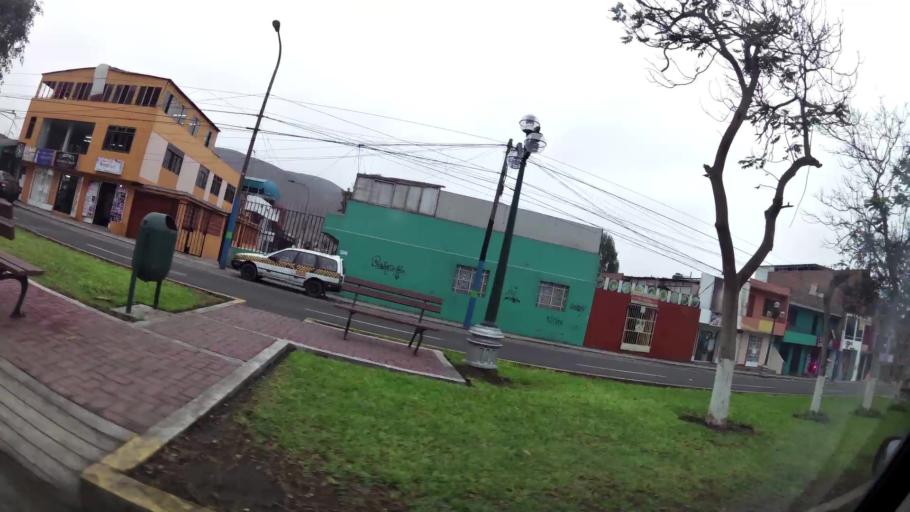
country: PE
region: Lima
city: Ventanilla
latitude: -11.8720
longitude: -77.1232
